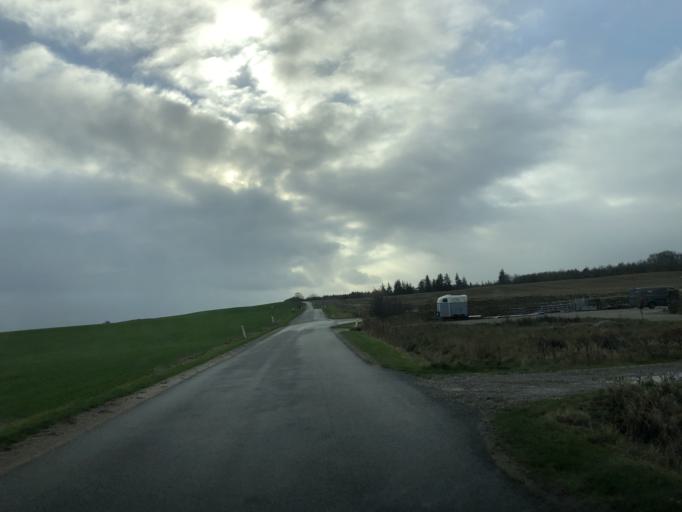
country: DK
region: North Denmark
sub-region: Rebild Kommune
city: Stovring
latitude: 56.9170
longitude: 9.7818
